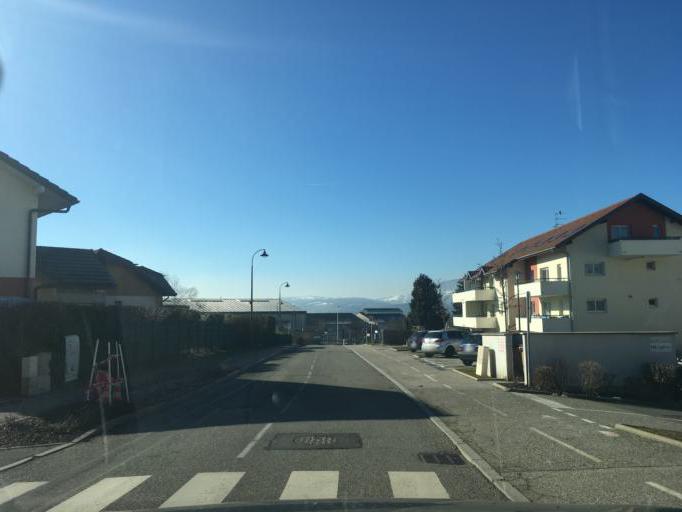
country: FR
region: Rhone-Alpes
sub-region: Departement de la Haute-Savoie
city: Cranves-Sales
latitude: 46.1905
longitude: 6.2888
